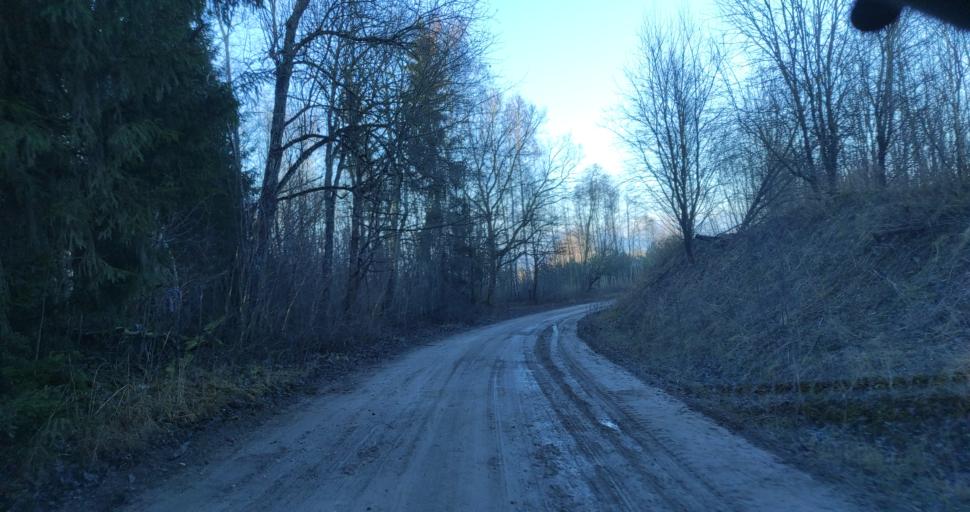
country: LV
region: Kuldigas Rajons
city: Kuldiga
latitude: 57.0469
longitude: 21.8640
